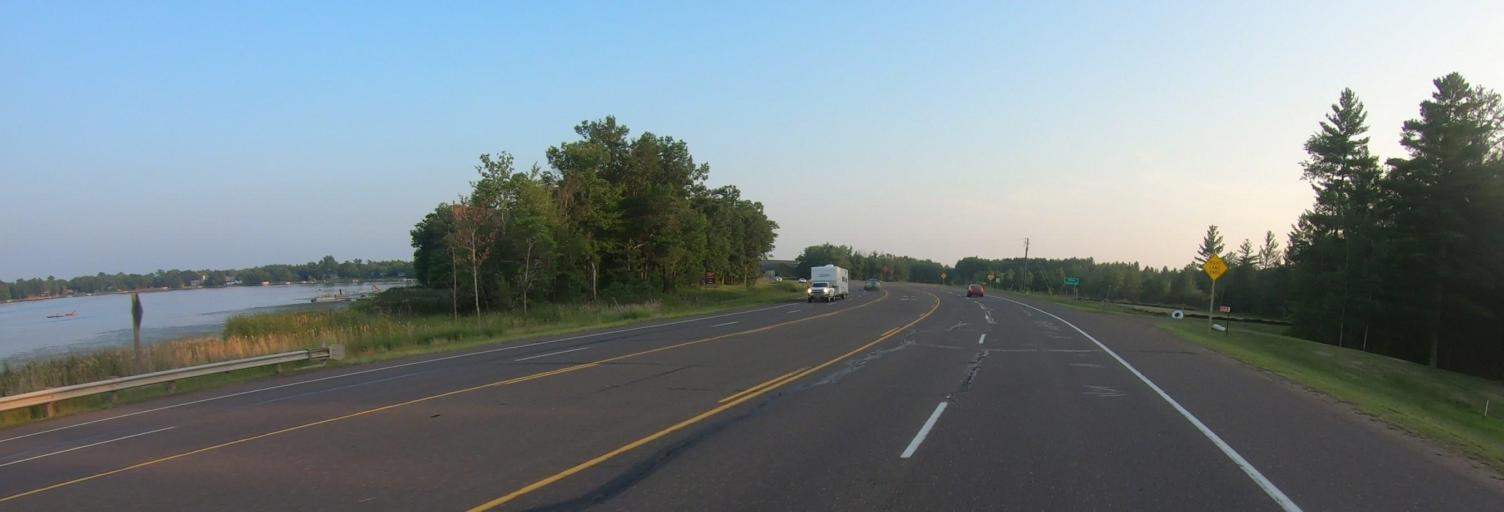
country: US
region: Wisconsin
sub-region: Burnett County
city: Siren
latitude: 45.7993
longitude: -92.3816
